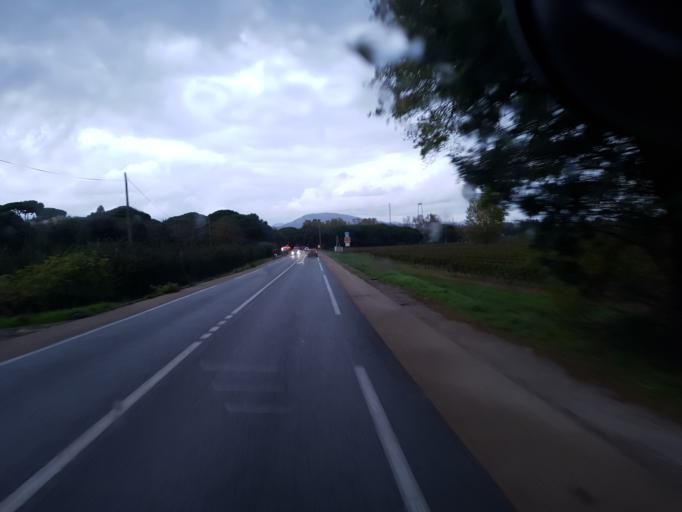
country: FR
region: Provence-Alpes-Cote d'Azur
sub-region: Departement du Var
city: Gassin
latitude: 43.2560
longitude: 6.5747
